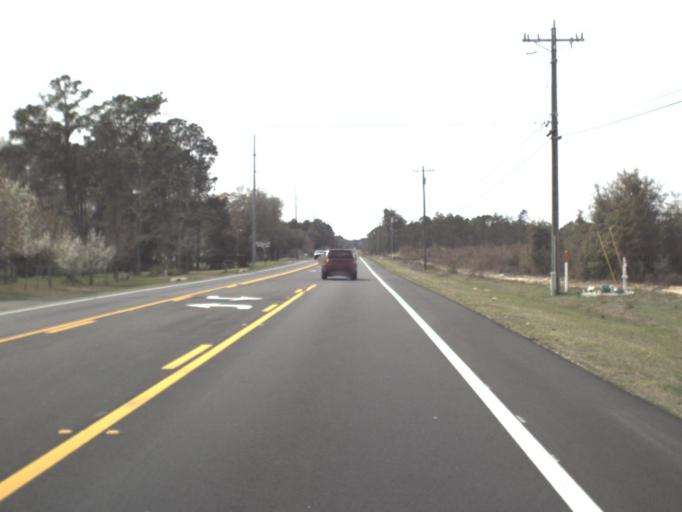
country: US
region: Florida
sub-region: Gadsden County
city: Midway
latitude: 30.4422
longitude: -84.4272
